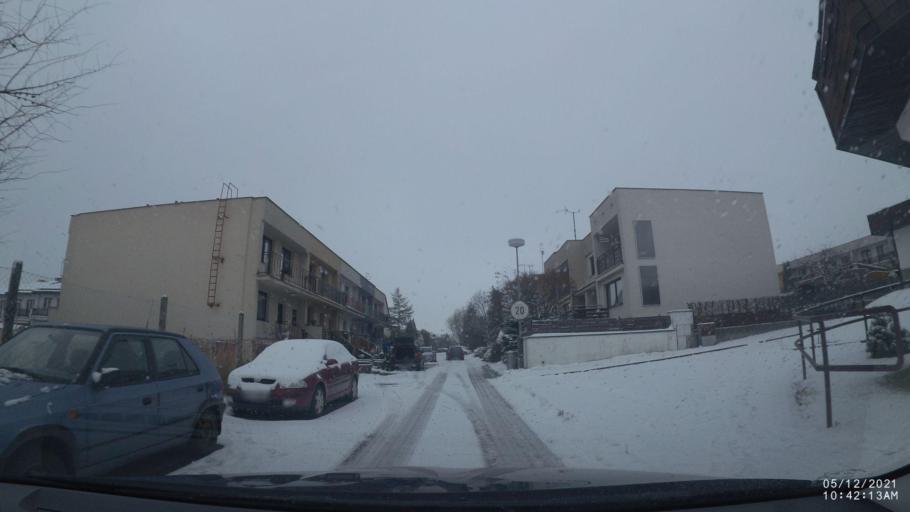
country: CZ
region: Kralovehradecky
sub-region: Okres Rychnov nad Kneznou
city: Rychnov nad Kneznou
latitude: 50.1660
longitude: 16.2860
